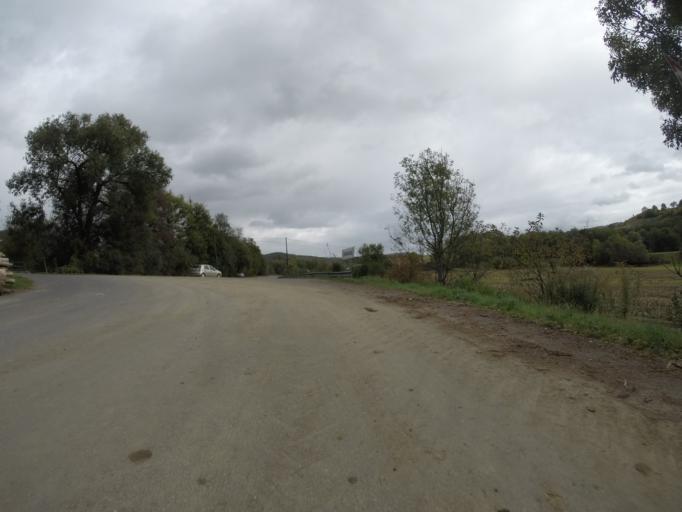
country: SK
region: Banskobystricky
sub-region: Okres Banska Bystrica
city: Zvolen
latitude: 48.5626
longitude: 19.0448
